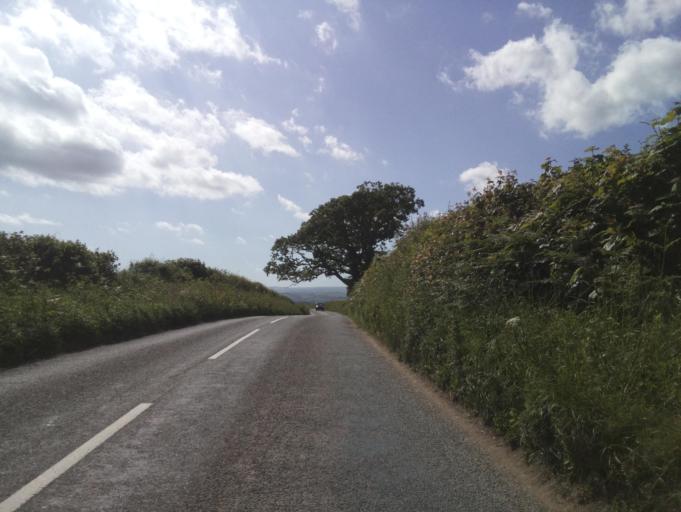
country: GB
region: England
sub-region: Devon
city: Marldon
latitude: 50.4415
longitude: -3.6349
